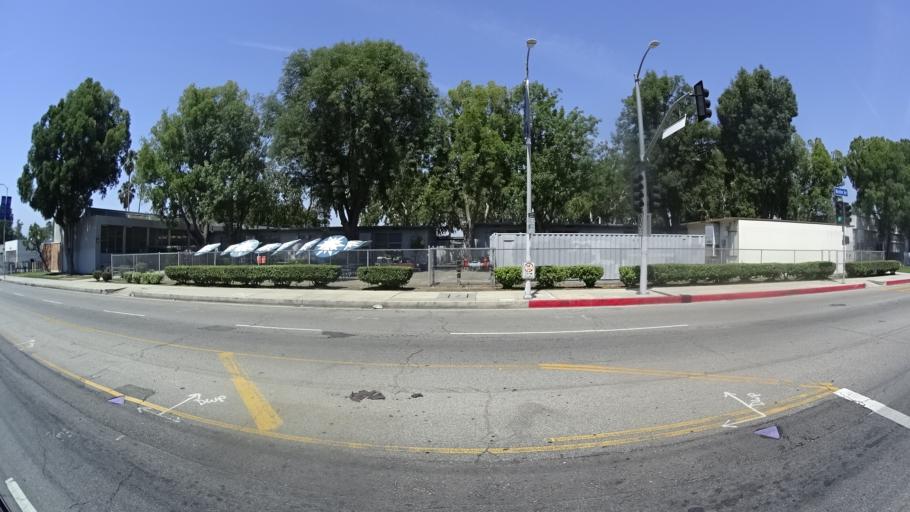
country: US
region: California
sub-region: Los Angeles County
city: Van Nuys
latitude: 34.2064
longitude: -118.4574
